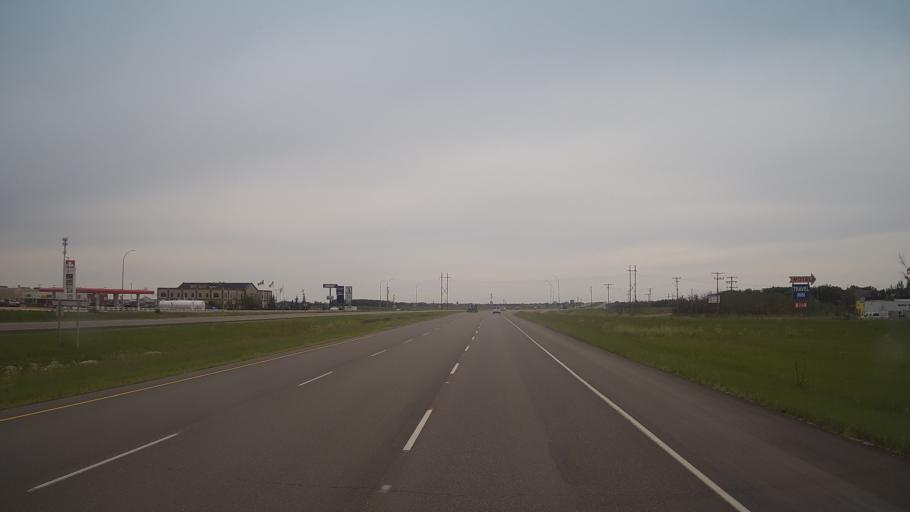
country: CA
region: Saskatchewan
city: Saskatoon
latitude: 52.0556
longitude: -106.5983
